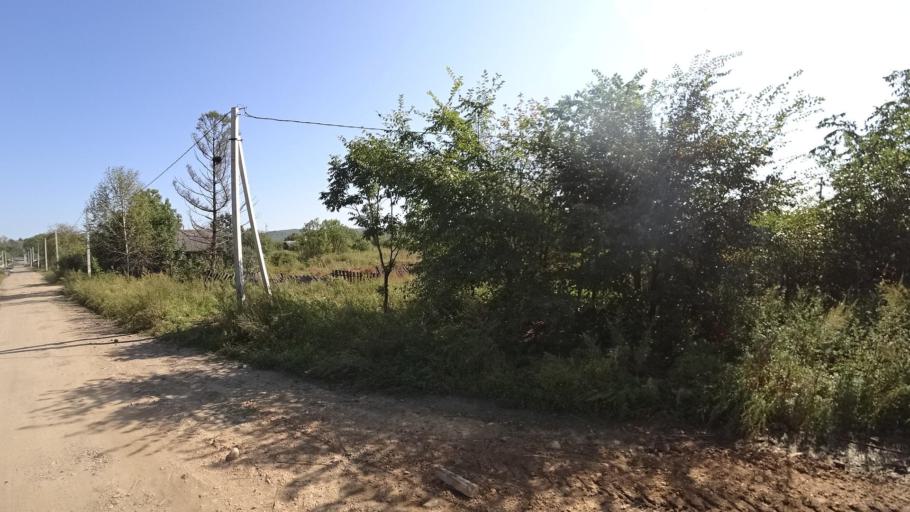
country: RU
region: Jewish Autonomous Oblast
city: Bira
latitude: 48.9942
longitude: 132.4652
